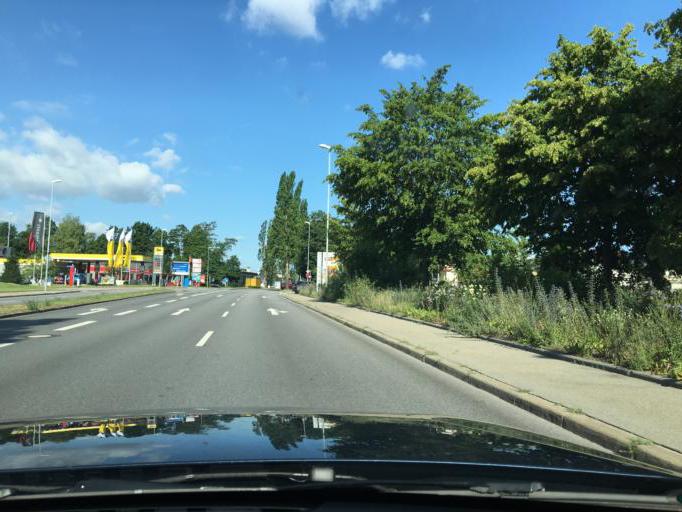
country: DE
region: Bavaria
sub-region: Upper Bavaria
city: Lenting
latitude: 48.7765
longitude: 11.4567
